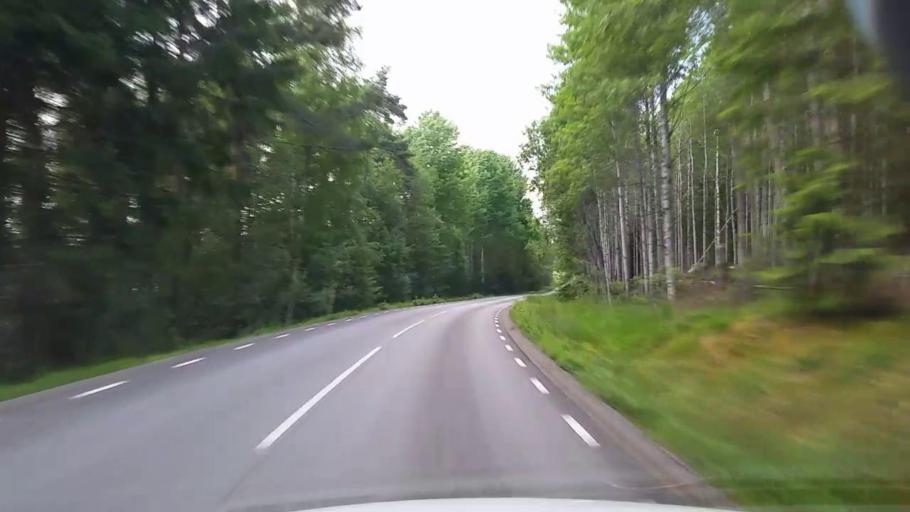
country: SE
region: Vaestmanland
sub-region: Kopings Kommun
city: Kolsva
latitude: 59.7557
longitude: 15.8334
